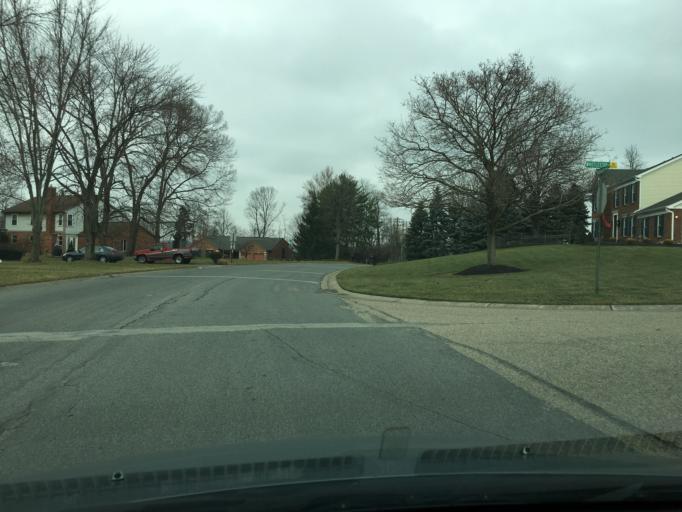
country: US
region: Ohio
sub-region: Hamilton County
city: Sharonville
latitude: 39.3113
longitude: -84.3994
